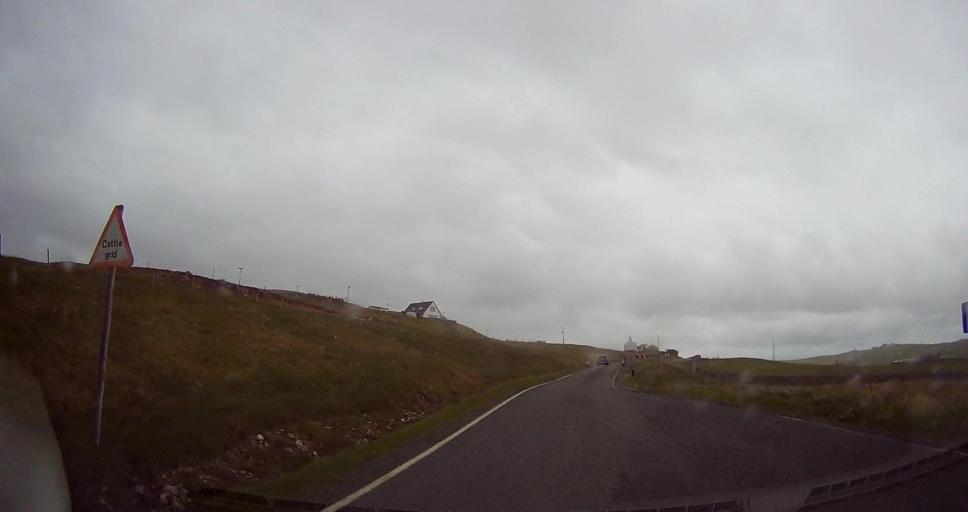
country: GB
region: Scotland
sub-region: Shetland Islands
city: Sandwick
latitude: 60.2446
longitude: -1.5288
